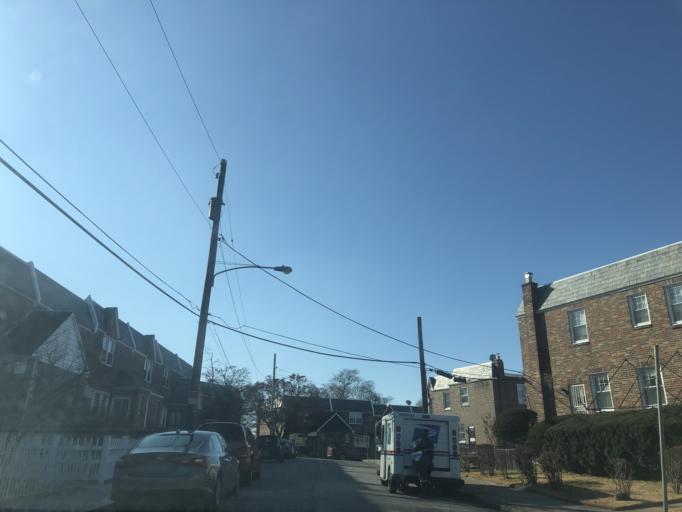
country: US
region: Pennsylvania
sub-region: Montgomery County
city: Bala-Cynwyd
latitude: 39.9906
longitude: -75.2236
